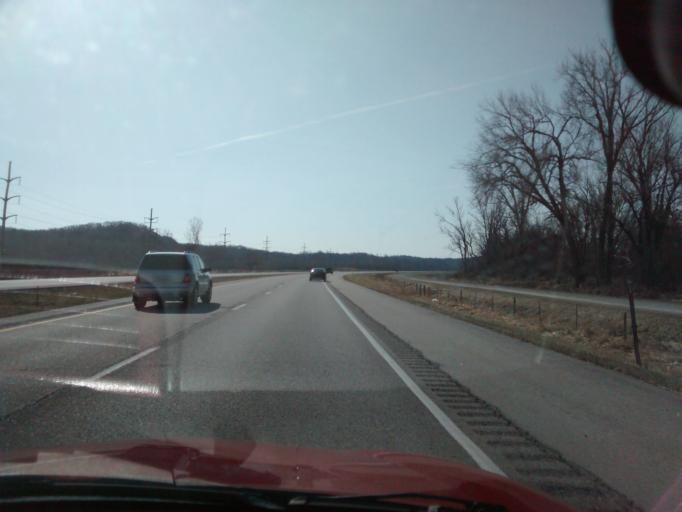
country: US
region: Iowa
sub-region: Pottawattamie County
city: Carter Lake
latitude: 41.3130
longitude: -95.8737
